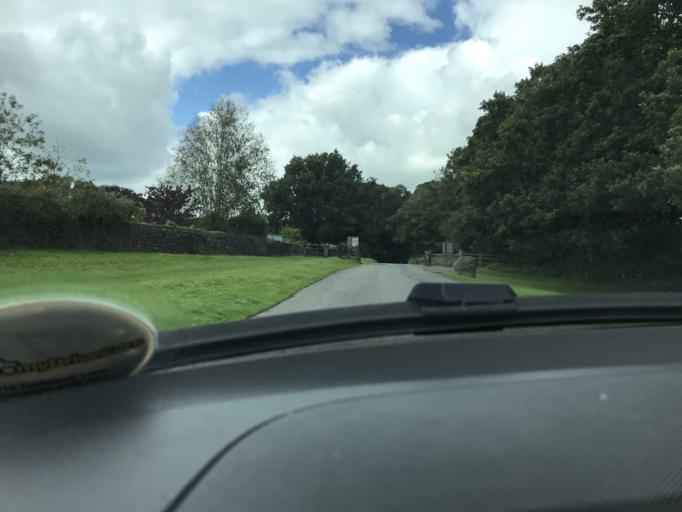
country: GB
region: England
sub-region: Devon
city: Tavistock
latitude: 50.5455
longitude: -4.1293
